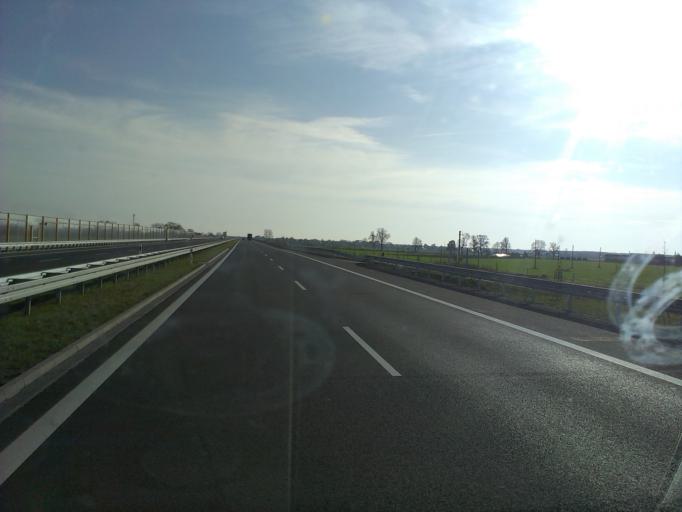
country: PL
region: Lubusz
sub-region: Powiat gorzowski
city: Deszczno
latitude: 52.6756
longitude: 15.2986
